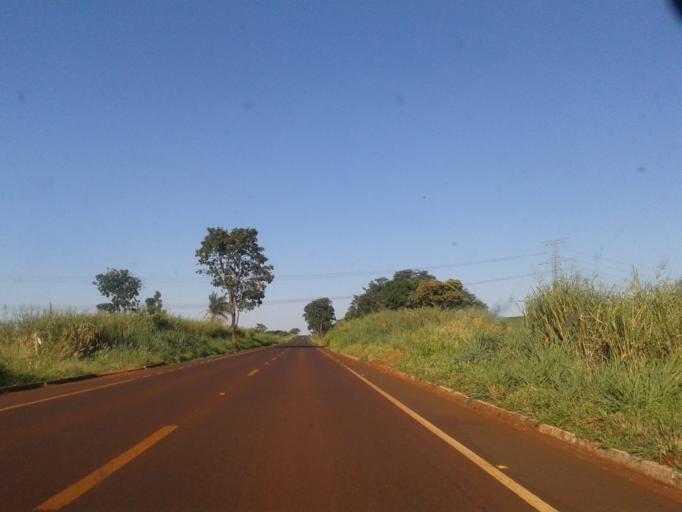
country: BR
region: Minas Gerais
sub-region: Capinopolis
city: Capinopolis
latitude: -18.7120
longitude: -49.7857
